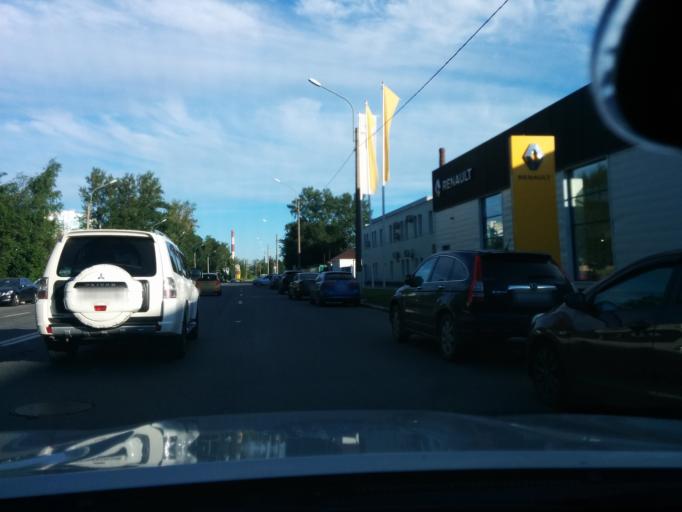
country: RU
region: St.-Petersburg
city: Kushelevka
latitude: 59.9825
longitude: 30.3640
